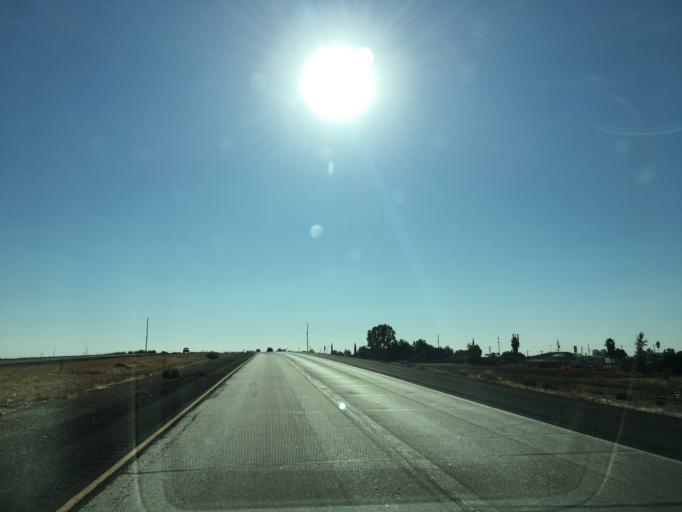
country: US
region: California
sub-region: Merced County
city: Dos Palos
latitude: 37.0516
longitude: -120.6392
